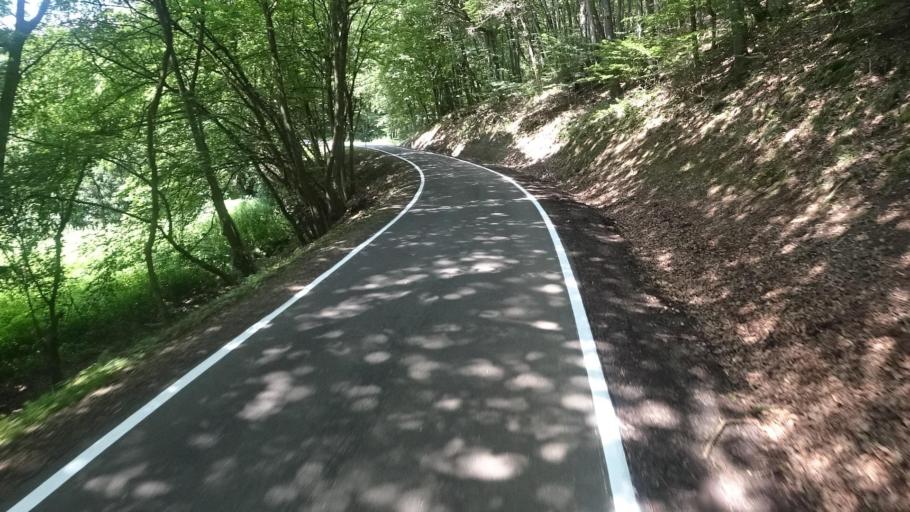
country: DE
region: Rheinland-Pfalz
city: Sankt Katharinen
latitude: 50.5818
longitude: 7.3553
